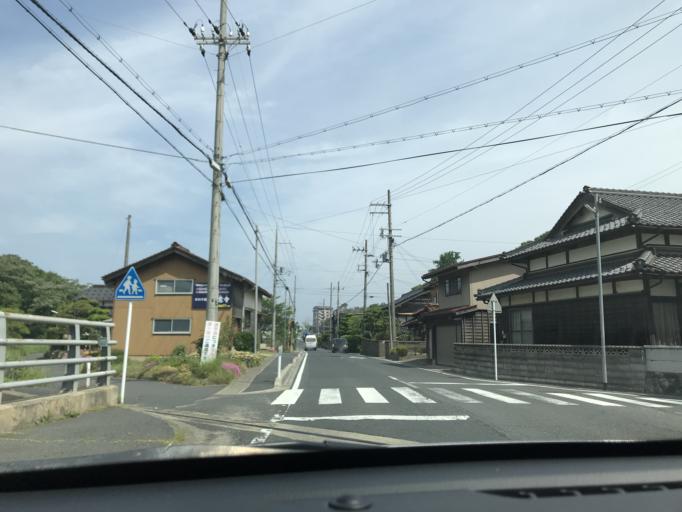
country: JP
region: Hyogo
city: Toyooka
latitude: 35.6536
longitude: 134.9697
